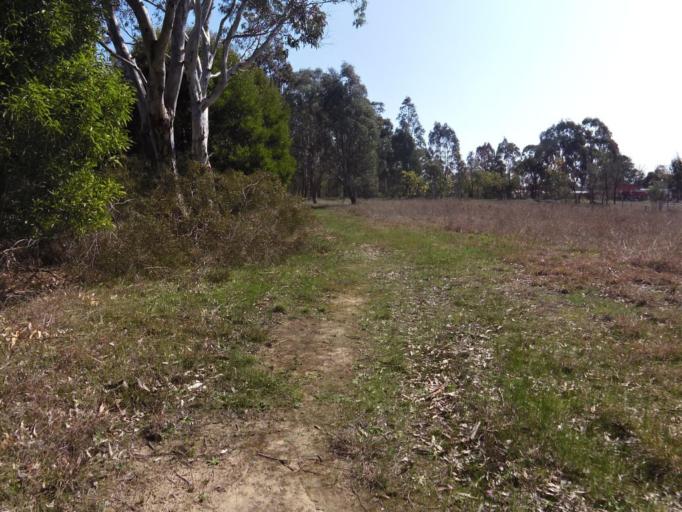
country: AU
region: Victoria
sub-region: Murrindindi
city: Alexandra
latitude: -36.9784
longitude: 145.7117
